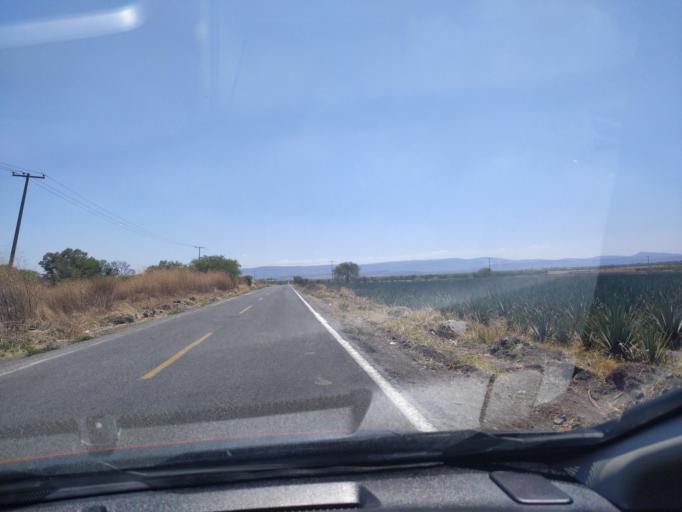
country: MX
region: Guanajuato
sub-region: San Francisco del Rincon
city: San Ignacio de Hidalgo
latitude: 20.7892
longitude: -101.8359
